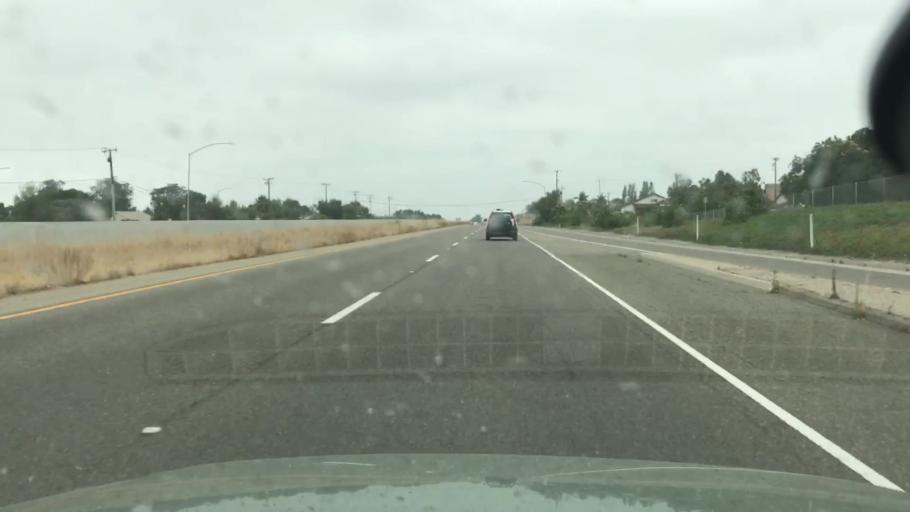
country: US
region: California
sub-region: Santa Barbara County
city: Orcutt
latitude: 34.8668
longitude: -120.4365
